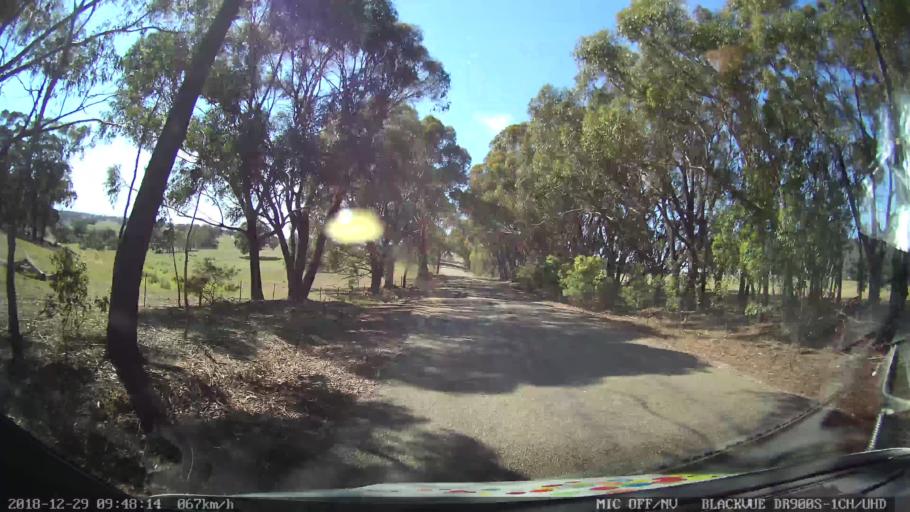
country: AU
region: New South Wales
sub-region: Upper Lachlan Shire
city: Crookwell
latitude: -34.7142
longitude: 149.4543
